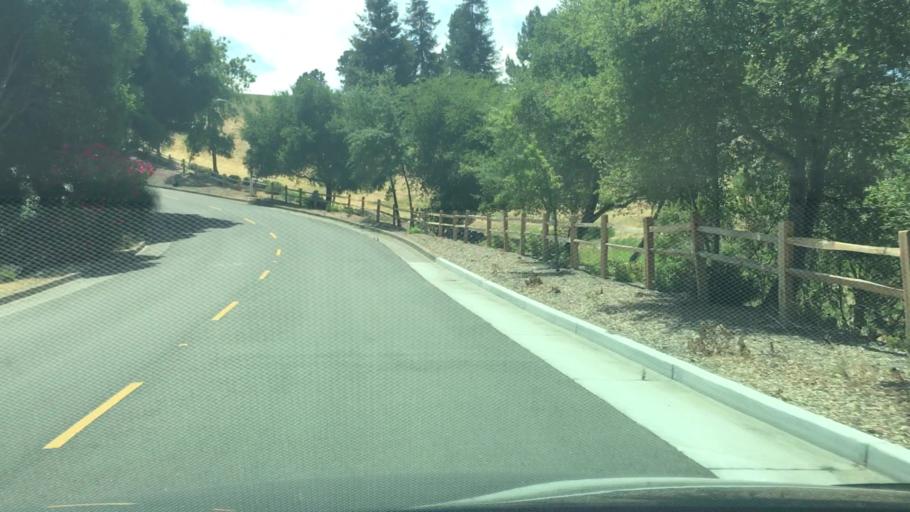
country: US
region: California
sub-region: Santa Clara County
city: Los Altos Hills
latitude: 37.3767
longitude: -122.1712
